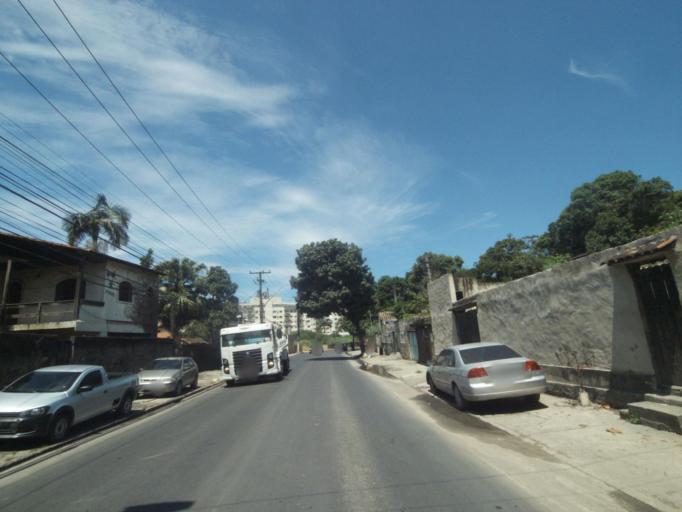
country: BR
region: Rio de Janeiro
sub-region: Sao Goncalo
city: Sao Goncalo
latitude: -22.9055
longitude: -42.9856
